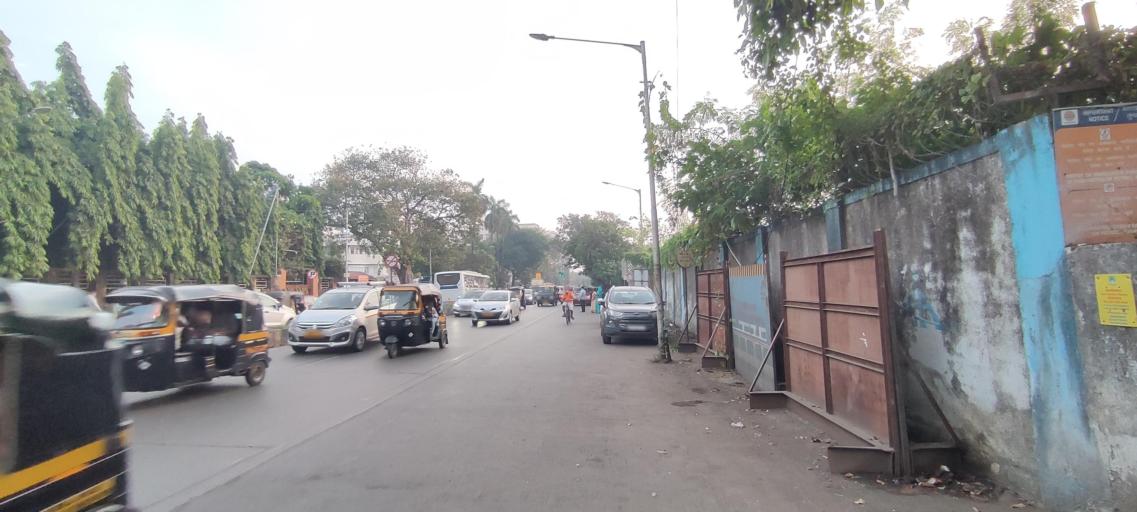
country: IN
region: Maharashtra
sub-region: Mumbai Suburban
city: Mumbai
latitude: 19.0970
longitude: 72.8395
